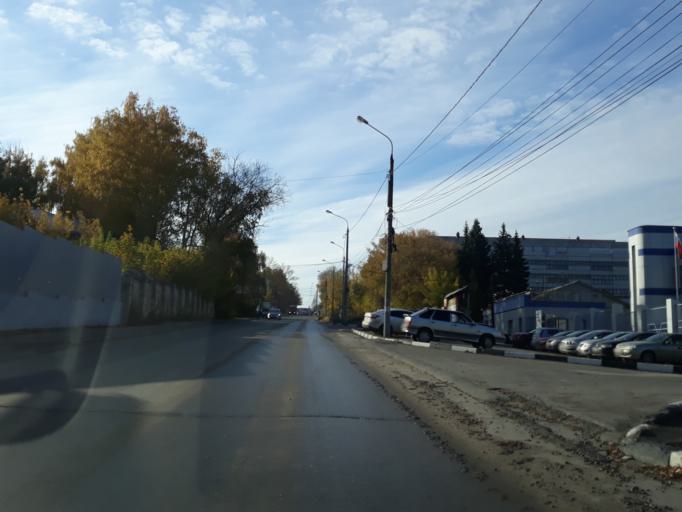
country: RU
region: Nizjnij Novgorod
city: Nizhniy Novgorod
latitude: 56.2473
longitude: 43.9866
